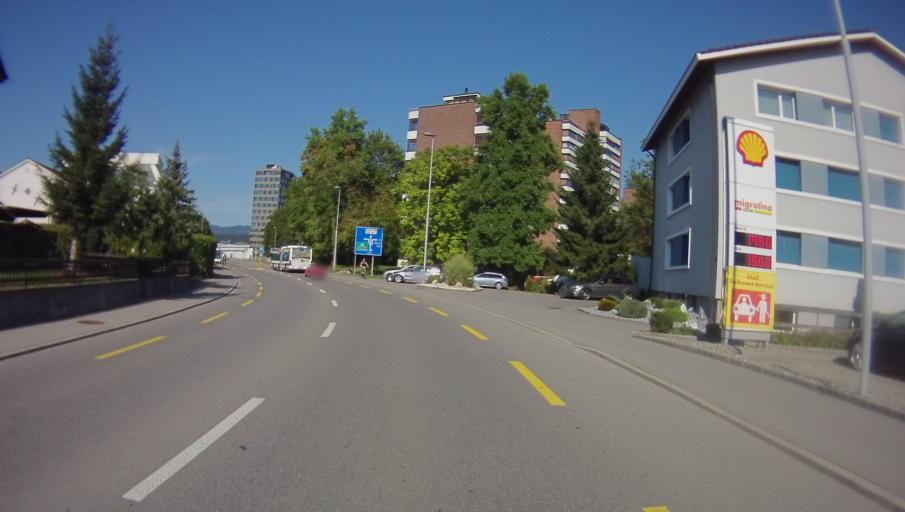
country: CH
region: Zug
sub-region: Zug
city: Cham
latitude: 47.1828
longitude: 8.4718
